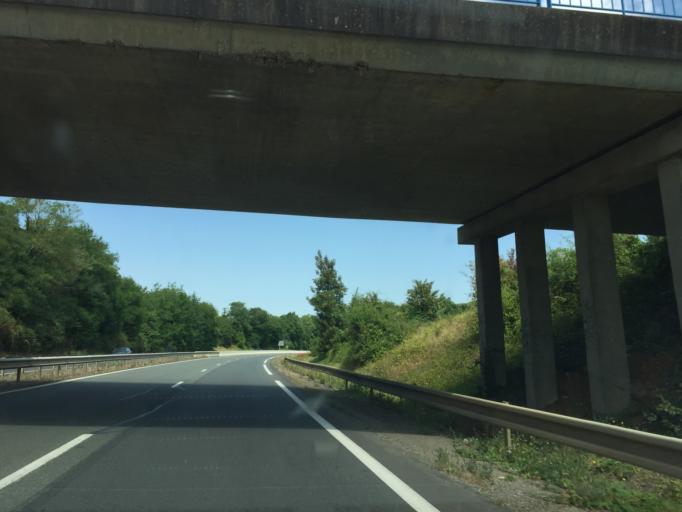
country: FR
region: Poitou-Charentes
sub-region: Departement de la Vienne
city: Biard
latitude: 46.5622
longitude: 0.3027
